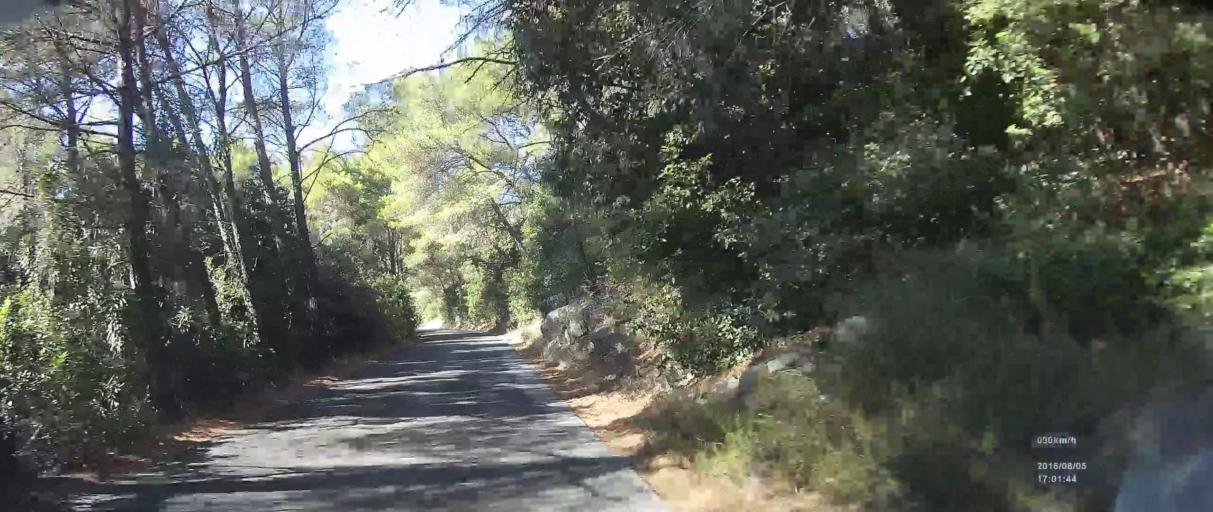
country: HR
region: Dubrovacko-Neretvanska
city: Blato
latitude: 42.7844
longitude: 17.3682
